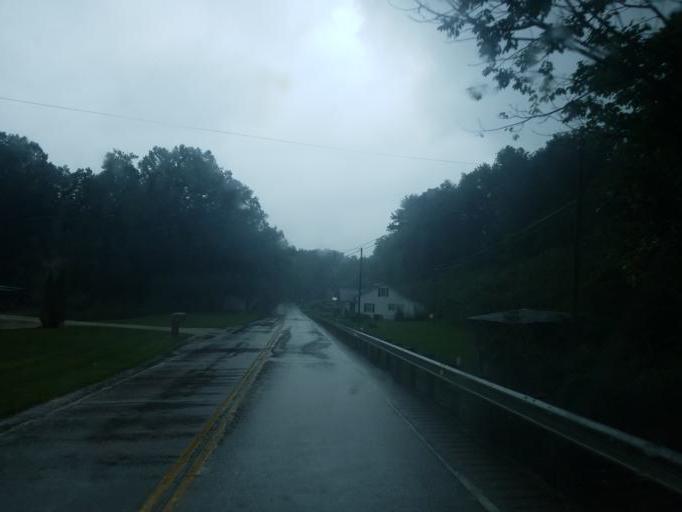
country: US
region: Kentucky
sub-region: Rowan County
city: Morehead
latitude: 38.2609
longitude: -83.3327
